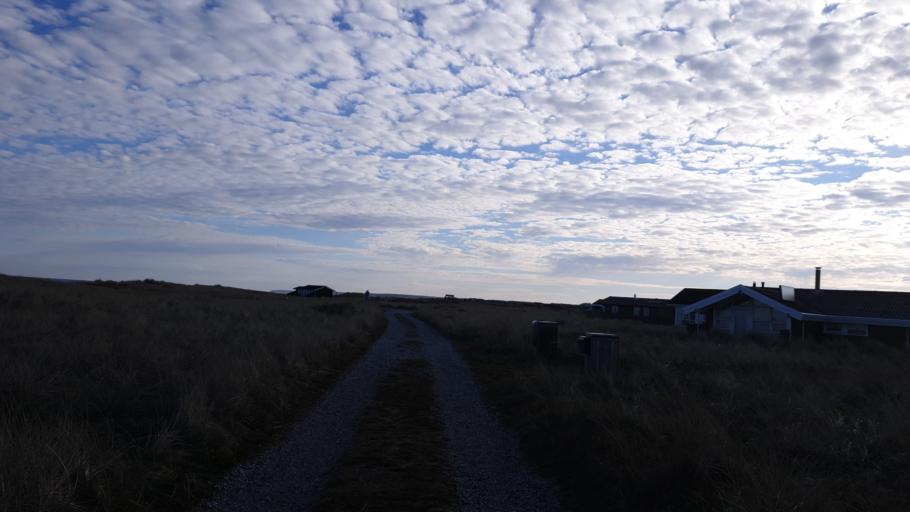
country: DK
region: North Denmark
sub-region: Hjorring Kommune
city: Hjorring
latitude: 57.4908
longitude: 9.8236
